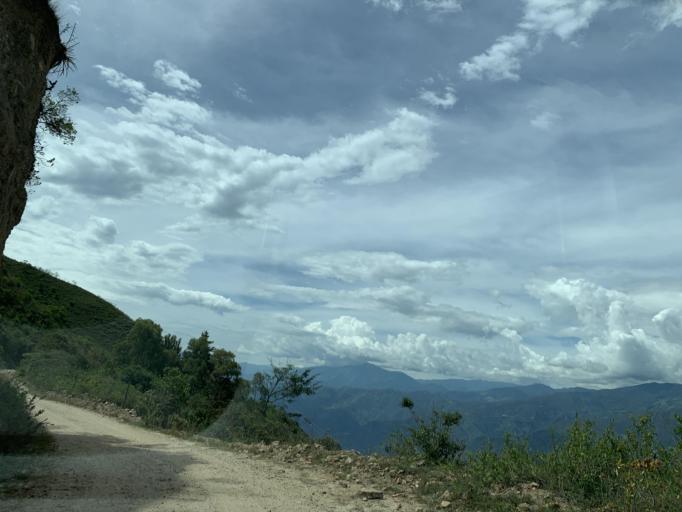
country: CO
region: Boyaca
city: Tipacoque
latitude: 6.4465
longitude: -72.7062
